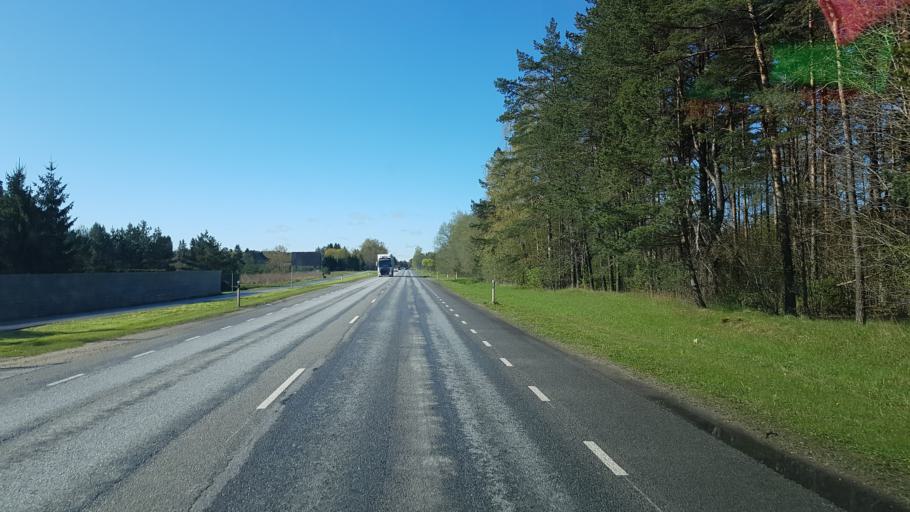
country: EE
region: Harju
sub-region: Kiili vald
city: Kiili
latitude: 59.3442
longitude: 24.7742
